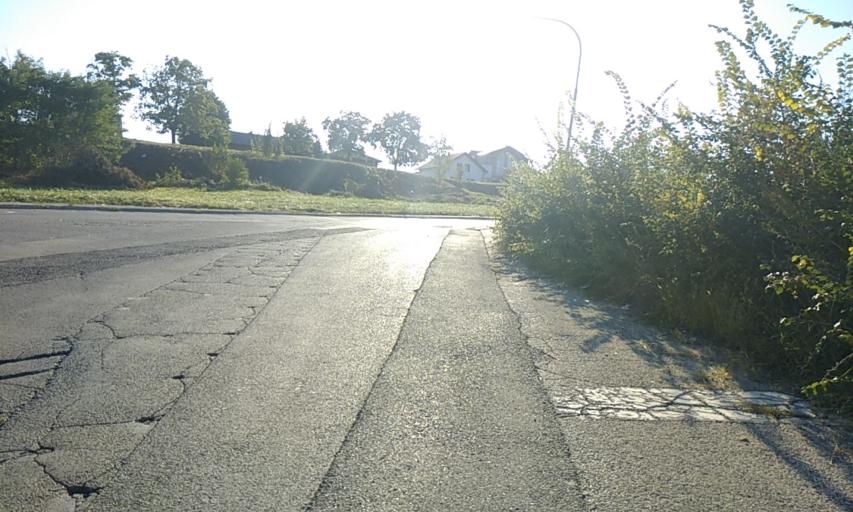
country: BA
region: Republika Srpska
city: Banja Luka
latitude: 44.7854
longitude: 17.1752
